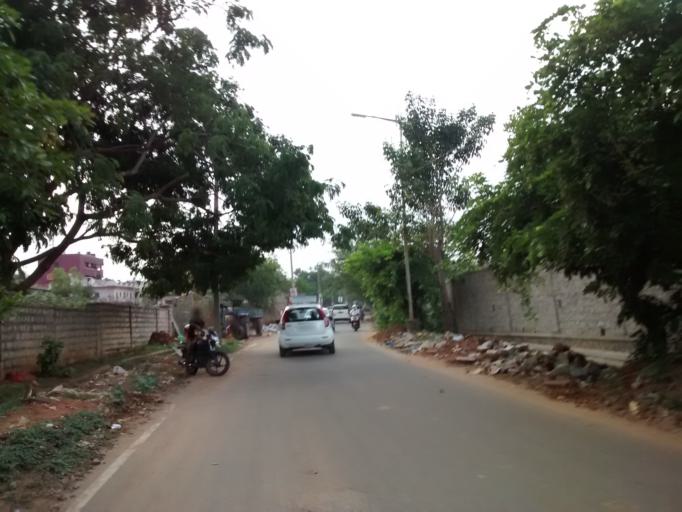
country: IN
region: Karnataka
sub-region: Bangalore Urban
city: Bangalore
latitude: 12.9647
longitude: 77.6687
